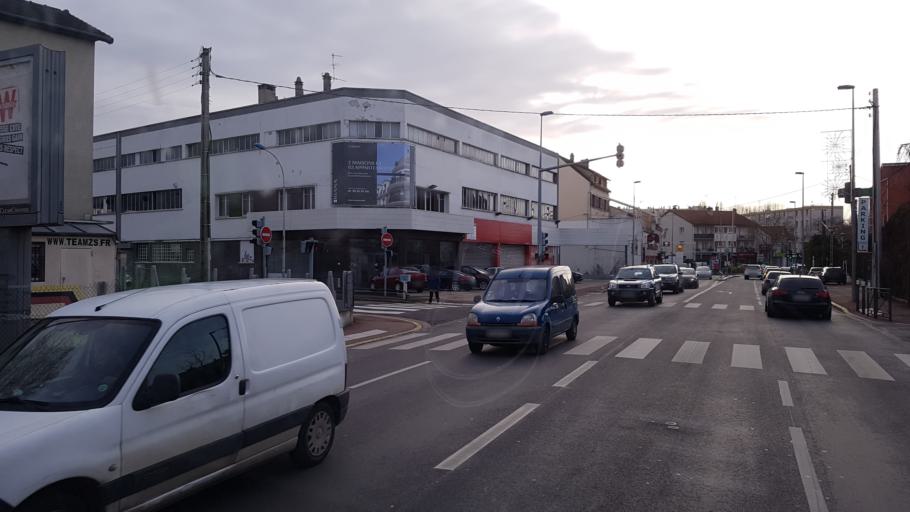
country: FR
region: Ile-de-France
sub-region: Departement de Seine-Saint-Denis
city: Le Blanc-Mesnil
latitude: 48.9246
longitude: 2.4639
